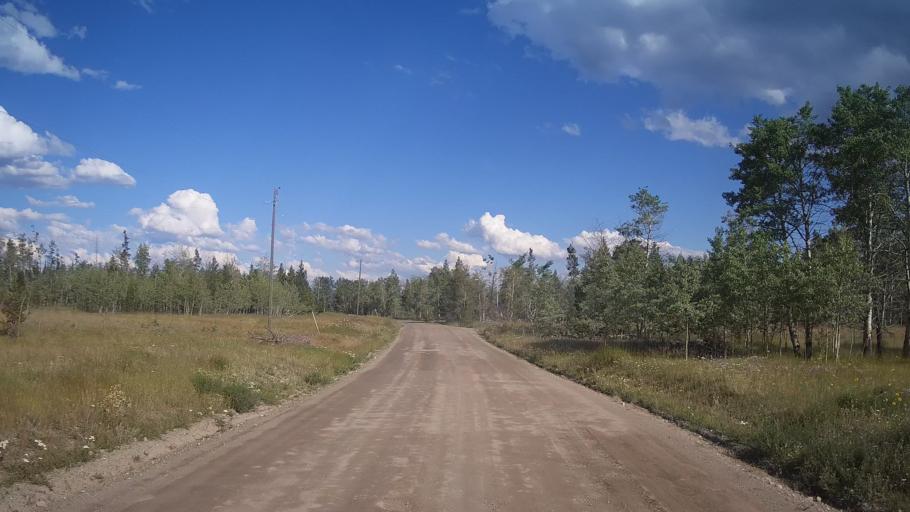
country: CA
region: British Columbia
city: Cache Creek
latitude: 51.2590
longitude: -121.6895
